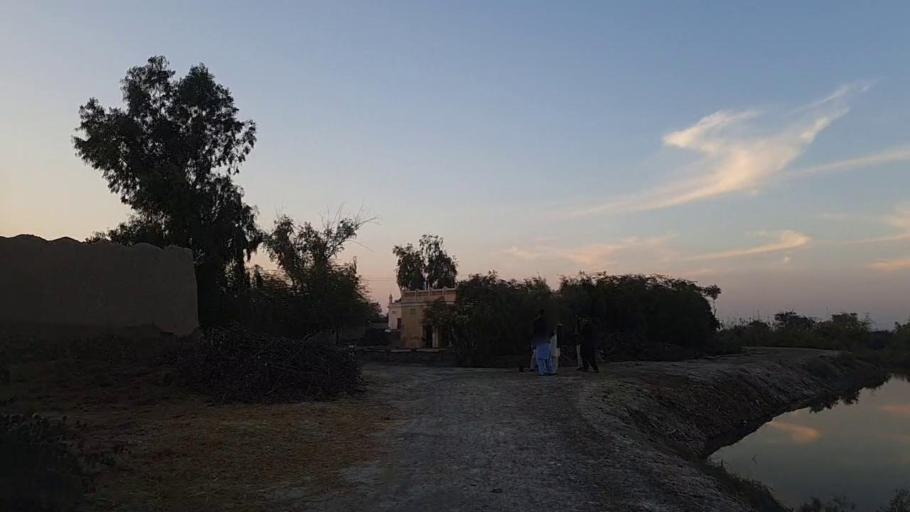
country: PK
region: Sindh
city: Bandhi
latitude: 26.5987
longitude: 68.3374
